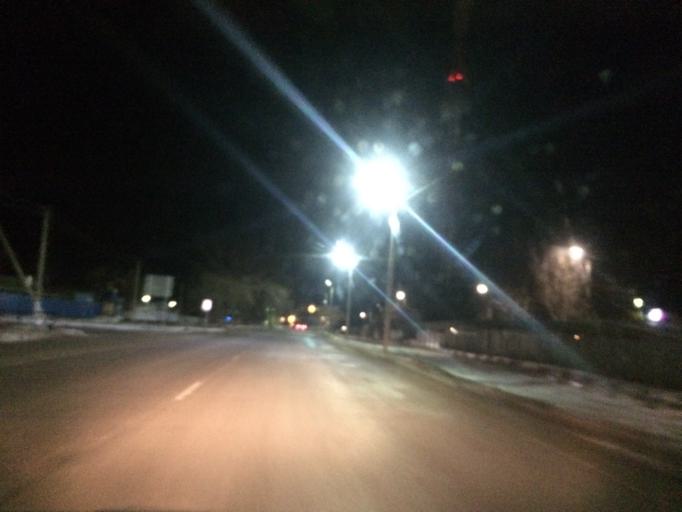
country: RU
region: Tula
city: Mendeleyevskiy
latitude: 54.1432
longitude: 37.5836
